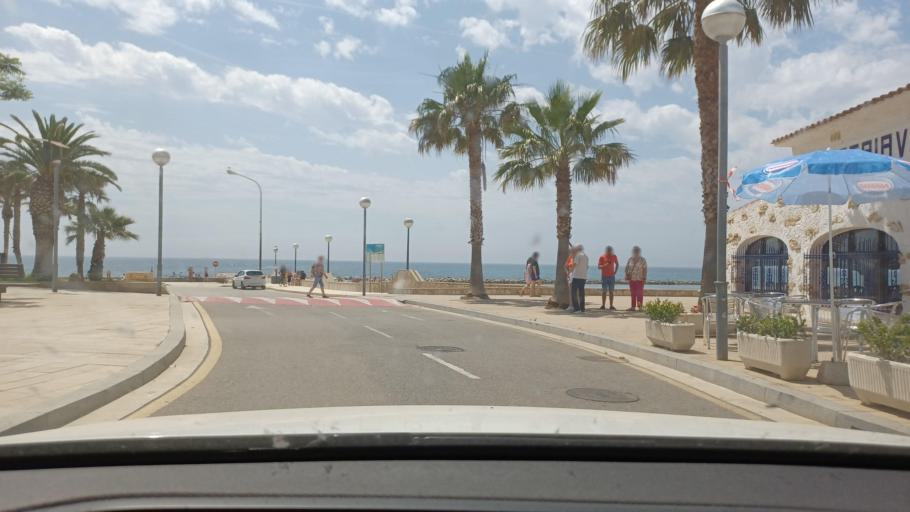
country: ES
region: Catalonia
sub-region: Provincia de Tarragona
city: Colldejou
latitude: 40.9889
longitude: 0.9233
